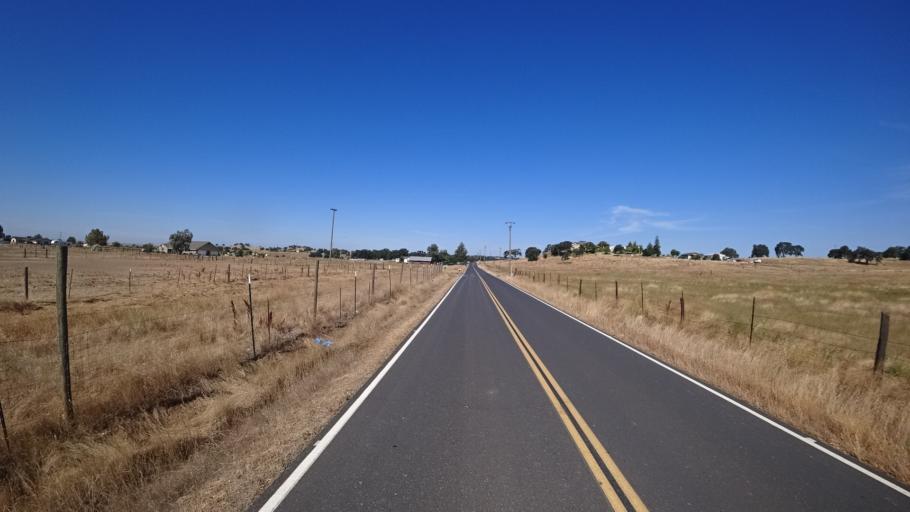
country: US
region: California
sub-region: Calaveras County
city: Rancho Calaveras
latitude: 38.0971
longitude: -120.9030
